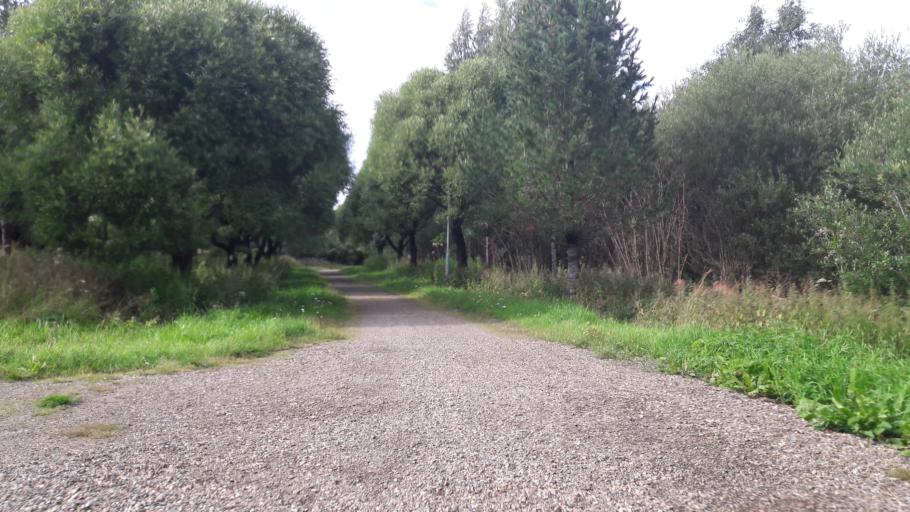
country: FI
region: North Karelia
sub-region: Joensuu
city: Joensuu
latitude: 62.5824
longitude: 29.8084
